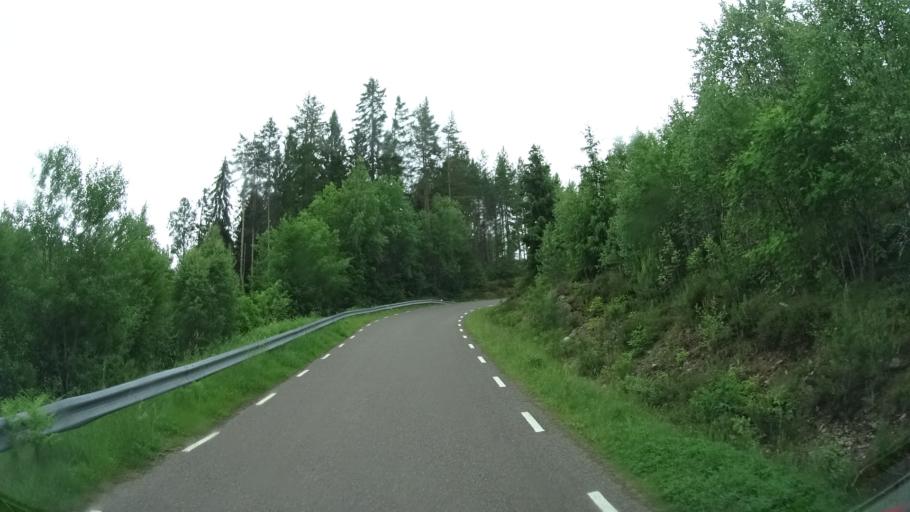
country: SE
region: Kalmar
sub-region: Vimmerby Kommun
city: Sodra Vi
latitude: 57.6977
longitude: 15.7300
